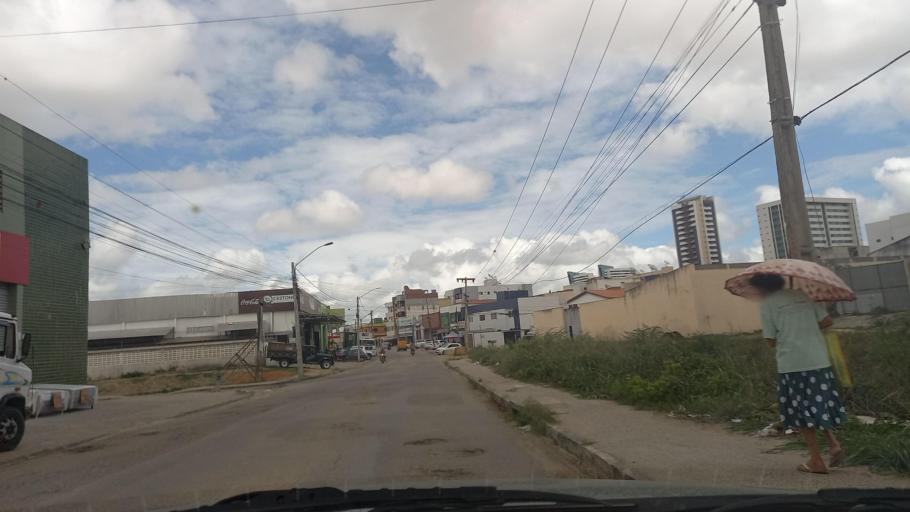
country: BR
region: Pernambuco
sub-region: Caruaru
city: Caruaru
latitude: -8.2667
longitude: -35.9611
